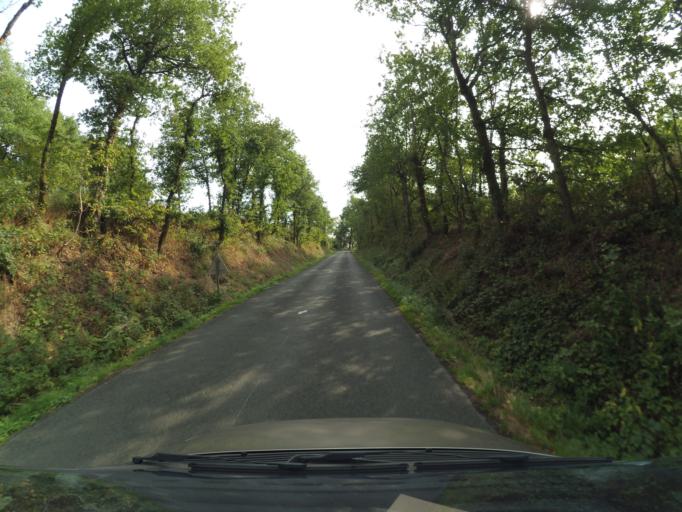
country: FR
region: Pays de la Loire
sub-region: Departement de Maine-et-Loire
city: Torfou
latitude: 47.0274
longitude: -1.1518
